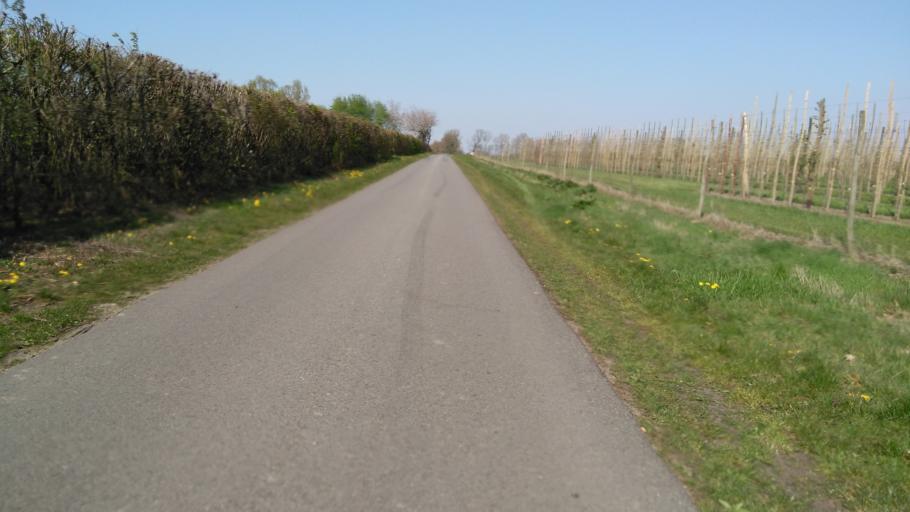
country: DE
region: Lower Saxony
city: Bliedersdorf
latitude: 53.4667
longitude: 9.5666
